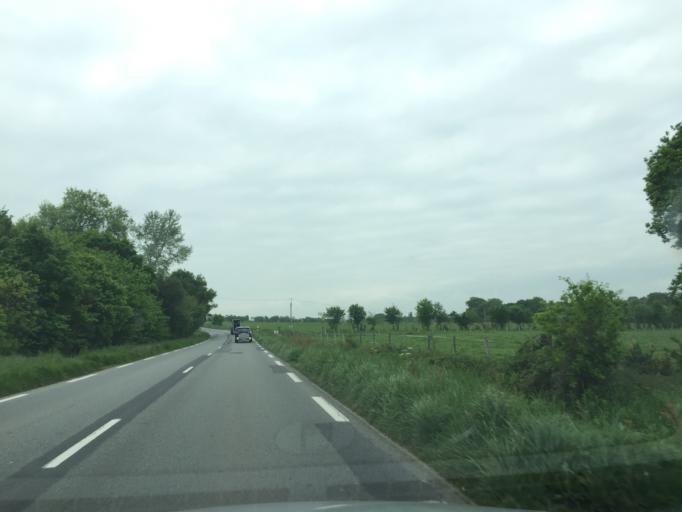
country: FR
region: Brittany
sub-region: Departement des Cotes-d'Armor
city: Lamballe
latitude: 48.4928
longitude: -2.4790
